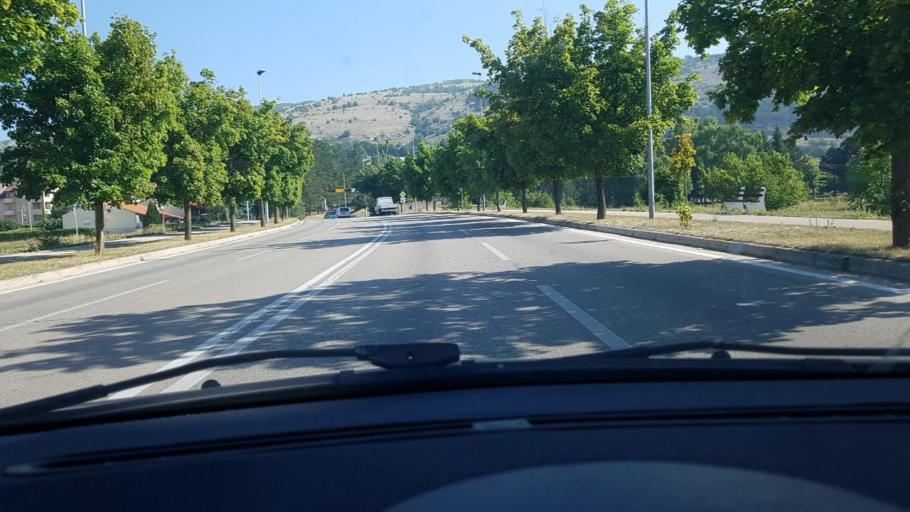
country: BA
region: Federation of Bosnia and Herzegovina
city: Livno
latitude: 43.8277
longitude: 16.9973
